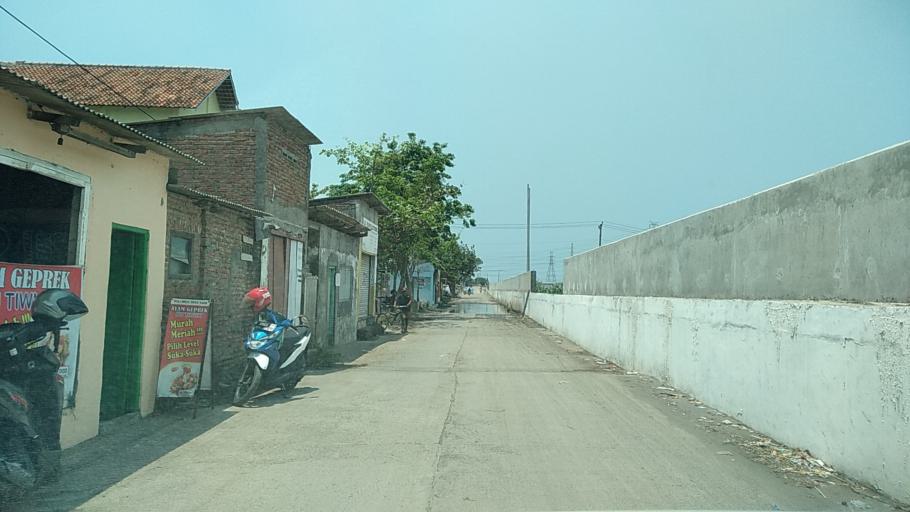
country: ID
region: Central Java
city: Semarang
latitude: -6.9573
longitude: 110.4412
